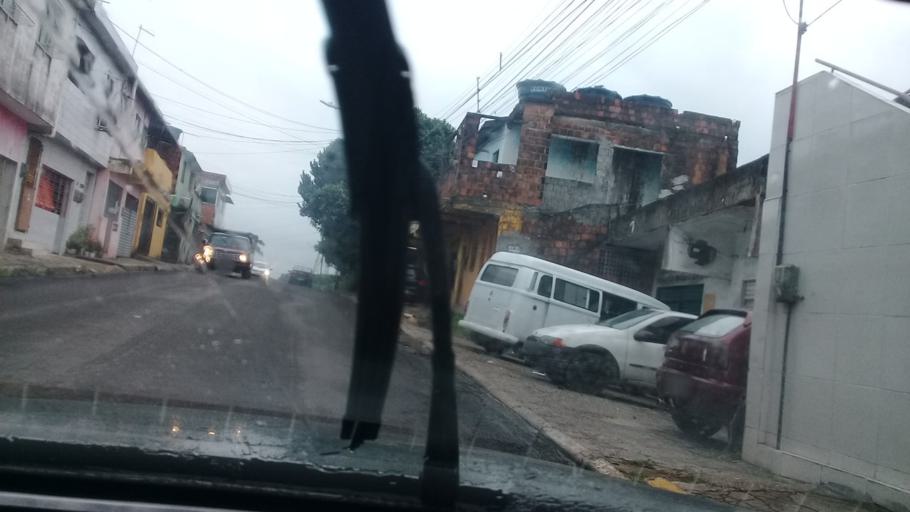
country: BR
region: Pernambuco
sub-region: Jaboatao Dos Guararapes
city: Jaboatao dos Guararapes
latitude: -8.0836
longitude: -34.9787
